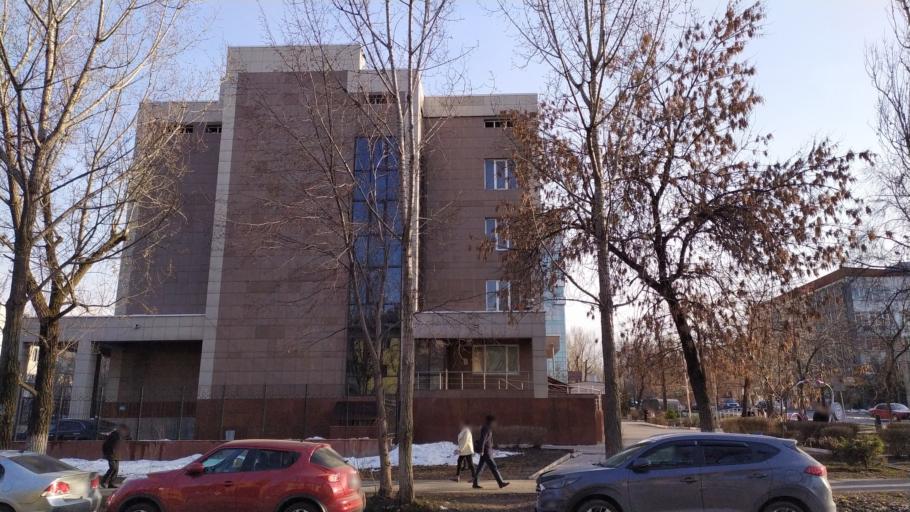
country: KZ
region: Almaty Qalasy
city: Almaty
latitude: 43.2221
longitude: 76.8972
